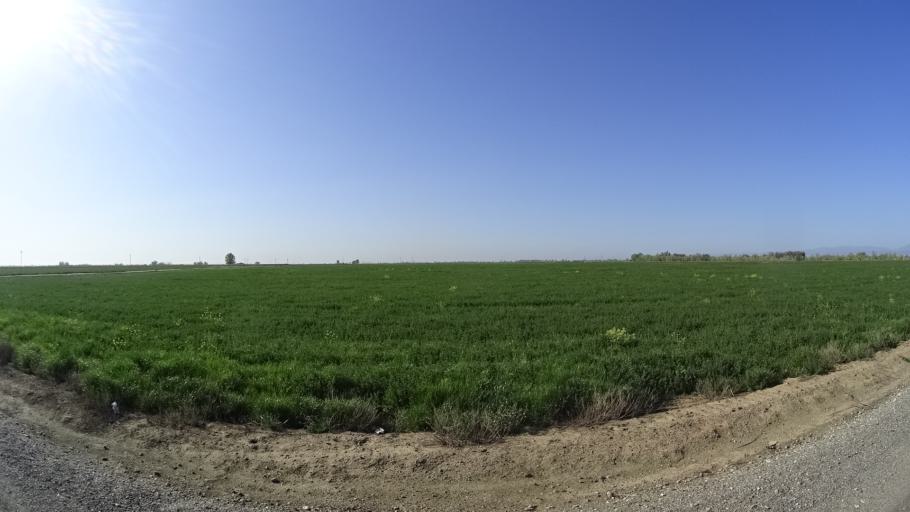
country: US
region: California
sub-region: Glenn County
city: Willows
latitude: 39.5533
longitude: -122.1535
